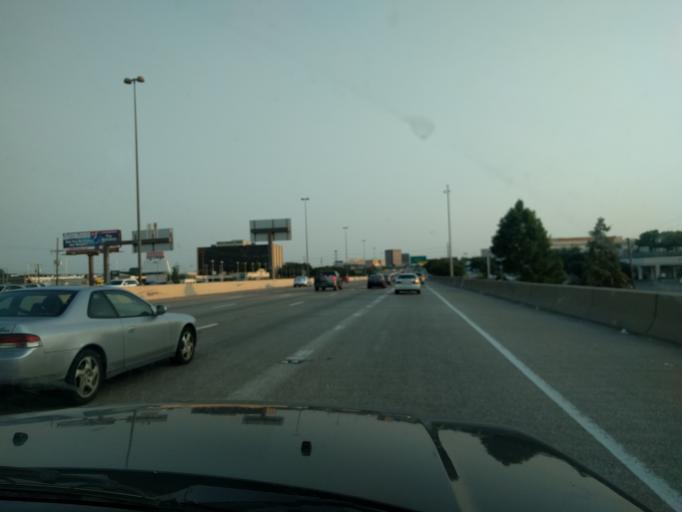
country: US
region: Texas
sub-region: Dallas County
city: Richardson
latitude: 32.9045
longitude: -96.7692
